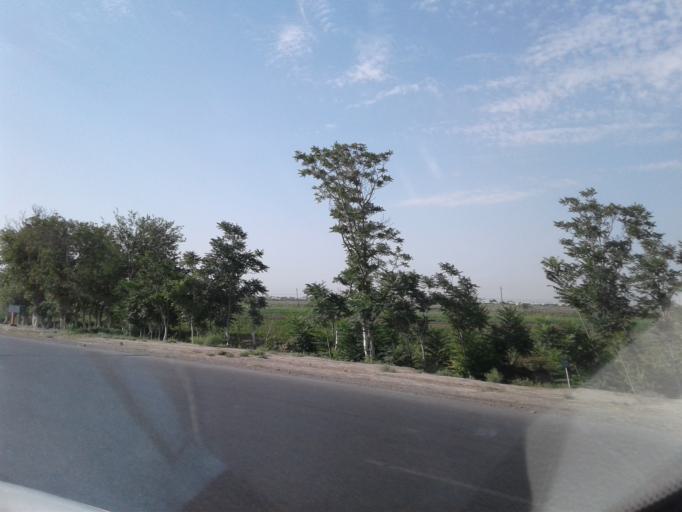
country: TM
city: Murgab
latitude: 37.5299
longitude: 61.8974
